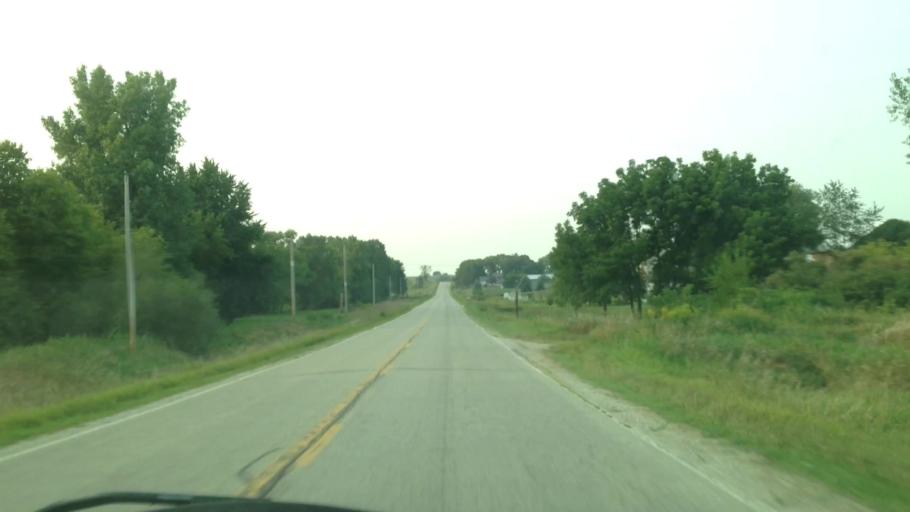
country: US
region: Iowa
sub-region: Iowa County
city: Marengo
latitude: 41.8721
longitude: -92.0889
